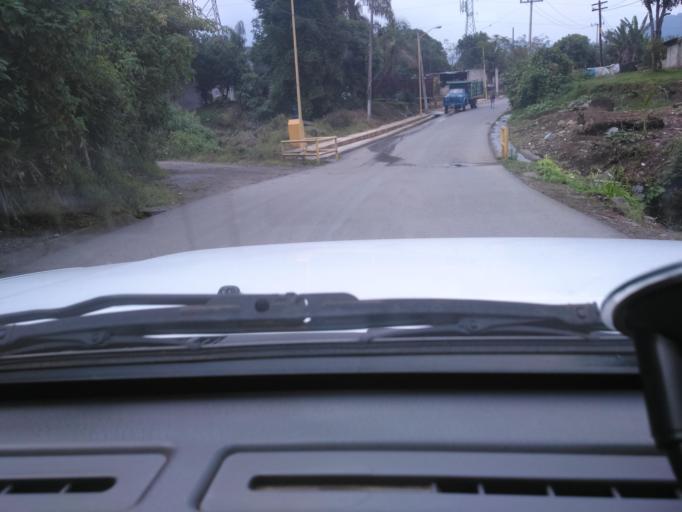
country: MX
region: Veracruz
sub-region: Mariano Escobedo
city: Chicola
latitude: 18.8945
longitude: -97.1084
